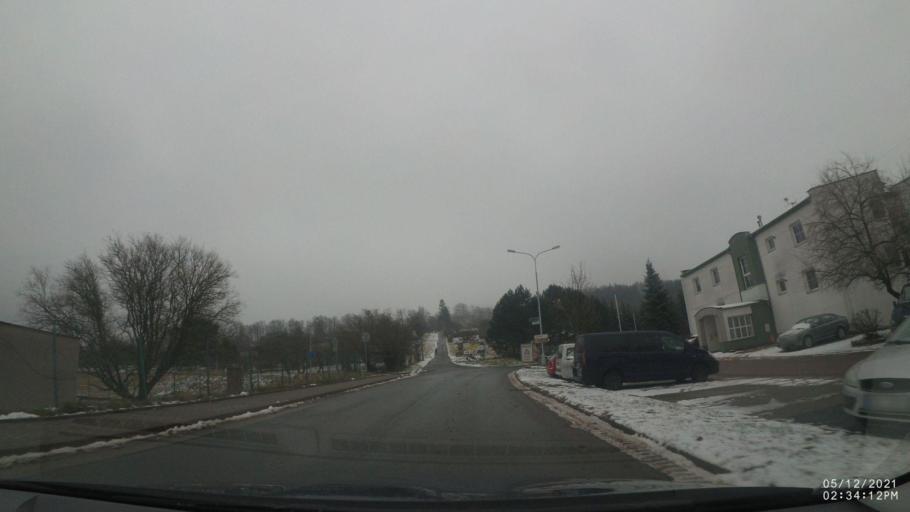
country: CZ
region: Kralovehradecky
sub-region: Okres Nachod
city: Nachod
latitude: 50.4055
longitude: 16.1656
